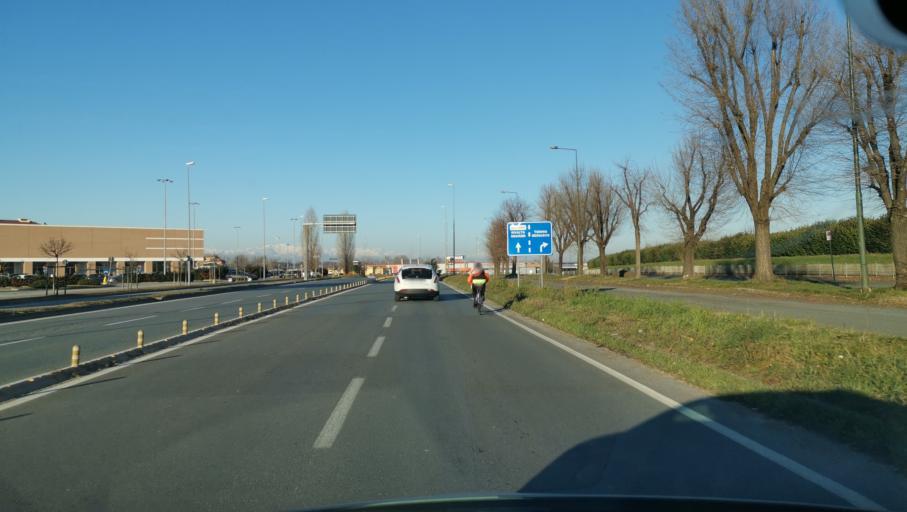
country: IT
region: Piedmont
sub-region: Provincia di Torino
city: Pasta
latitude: 45.0082
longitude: 7.5550
